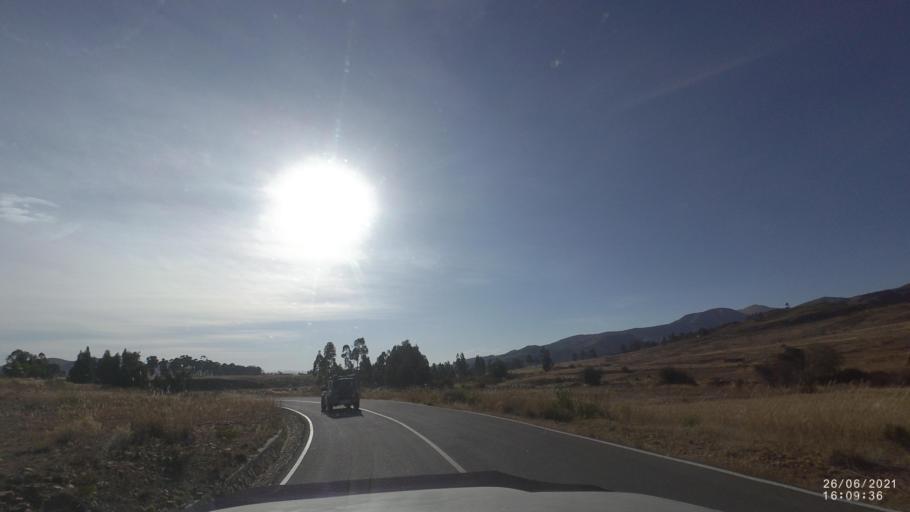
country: BO
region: Cochabamba
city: Arani
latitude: -17.8123
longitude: -65.7842
